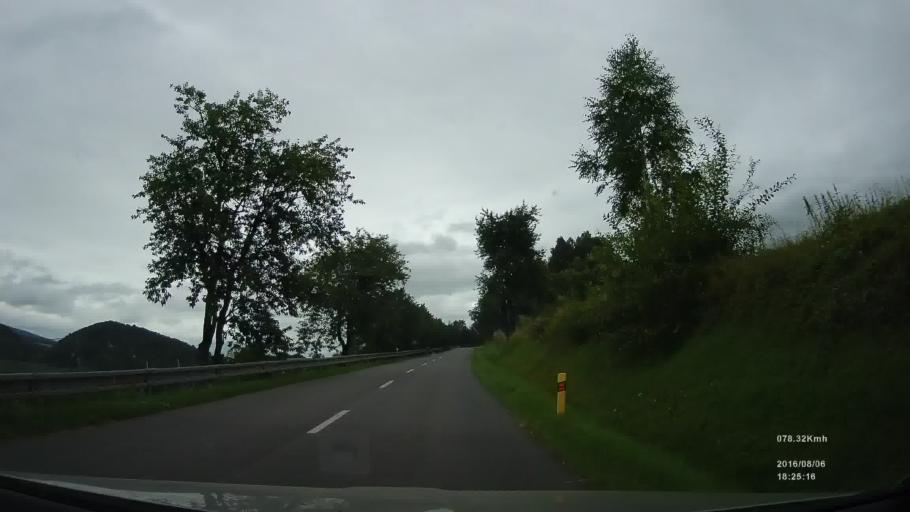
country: SK
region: Presovsky
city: Svidnik
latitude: 49.2917
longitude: 21.5733
